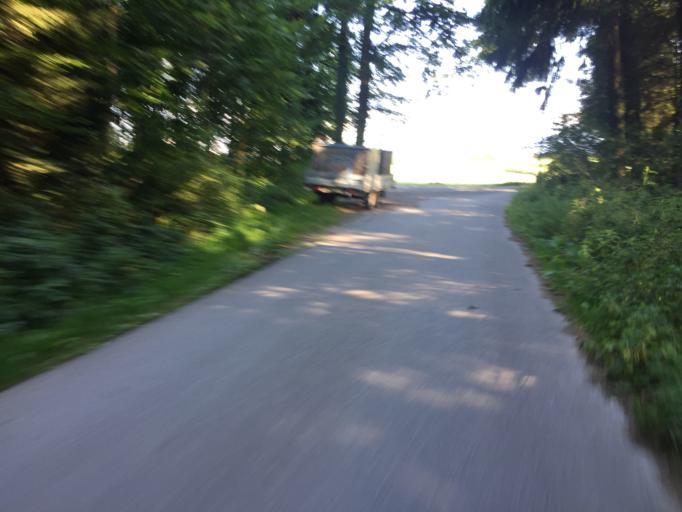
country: CH
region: Bern
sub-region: Bern-Mittelland District
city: Niederwichtrach
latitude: 46.8300
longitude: 7.5874
